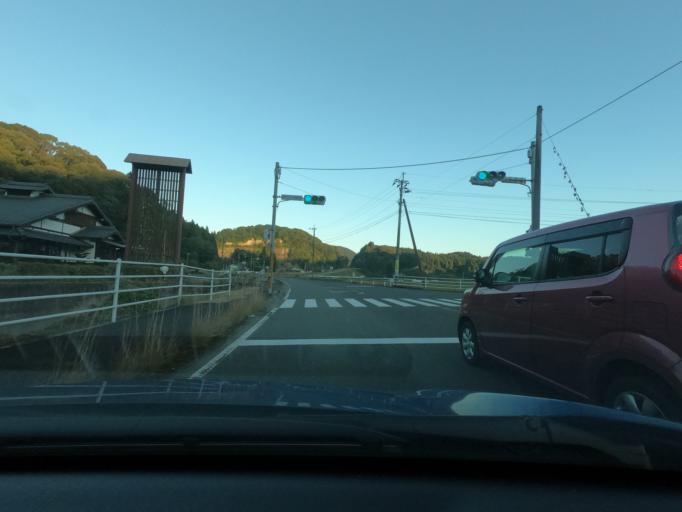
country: JP
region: Kagoshima
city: Satsumasendai
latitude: 31.8076
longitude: 130.3864
